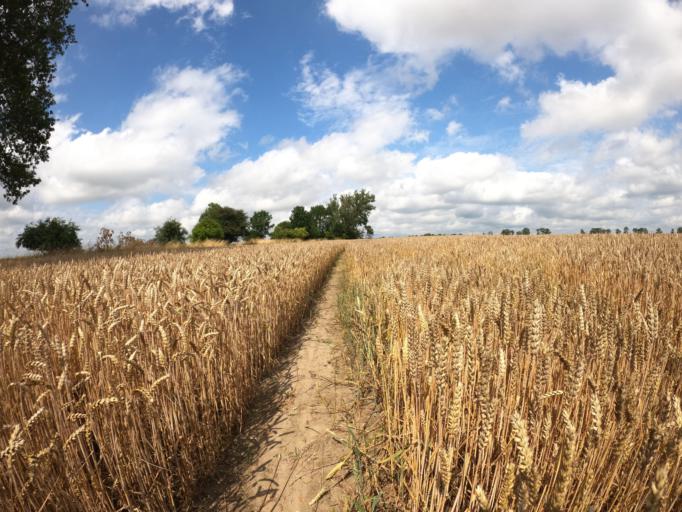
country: PL
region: West Pomeranian Voivodeship
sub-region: Powiat szczecinecki
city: Grzmiaca
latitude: 53.8068
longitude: 16.4697
